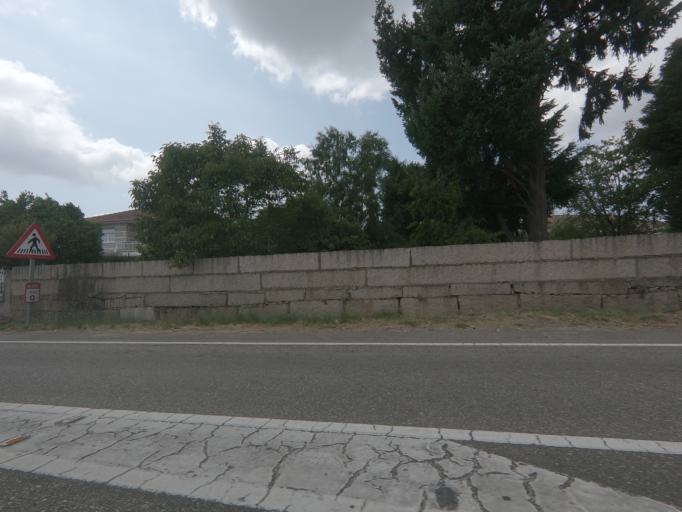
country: PT
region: Viana do Castelo
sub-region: Valenca
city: Valenca
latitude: 42.0342
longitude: -8.6611
